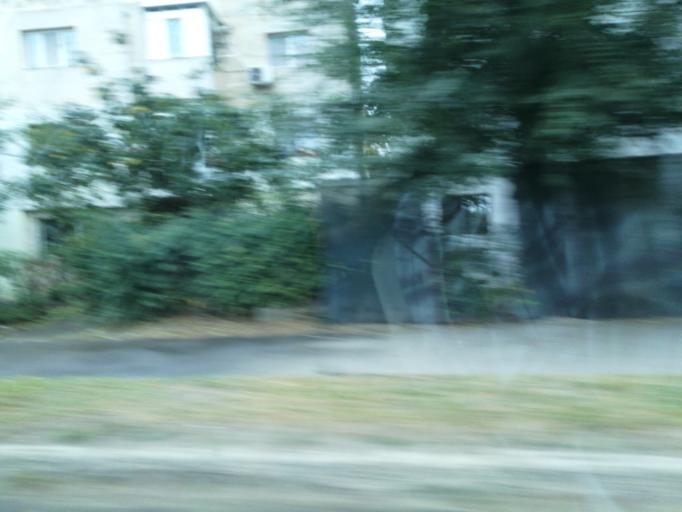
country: RO
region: Galati
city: Galati
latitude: 45.4566
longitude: 28.0166
